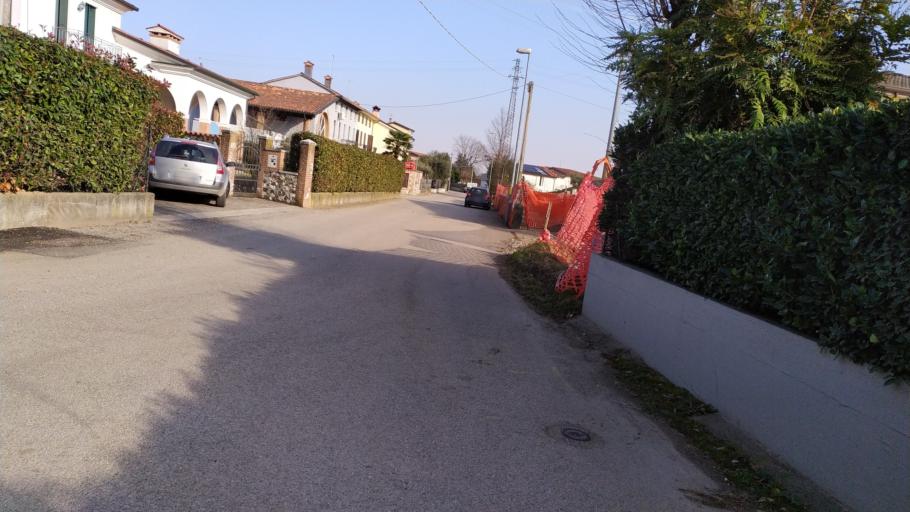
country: IT
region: Veneto
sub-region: Provincia di Vicenza
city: Marano Vicentino
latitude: 45.6913
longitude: 11.4178
